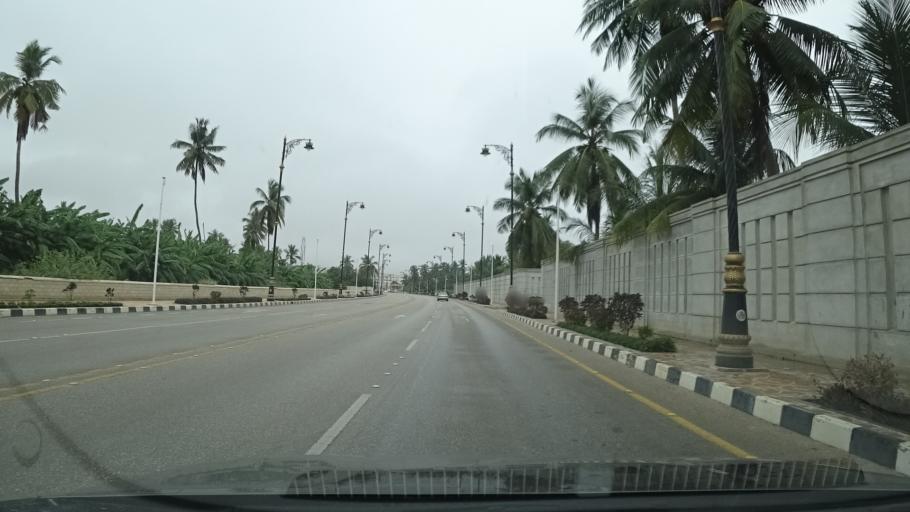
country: OM
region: Zufar
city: Salalah
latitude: 17.0050
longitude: 54.0965
